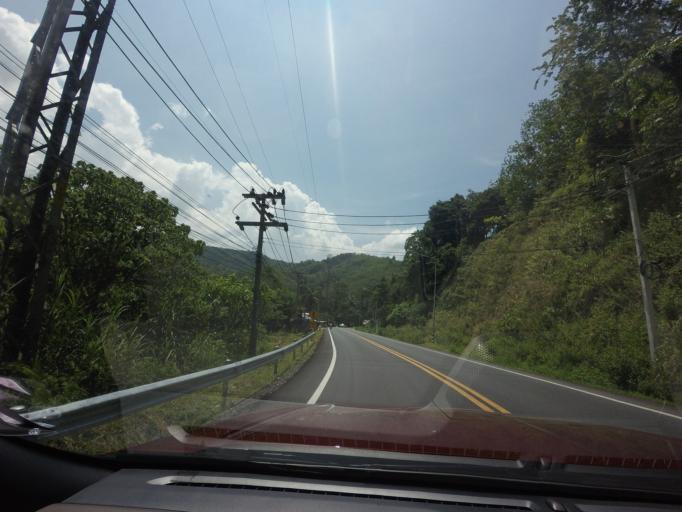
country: TH
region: Yala
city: Betong
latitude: 5.9093
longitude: 101.1522
